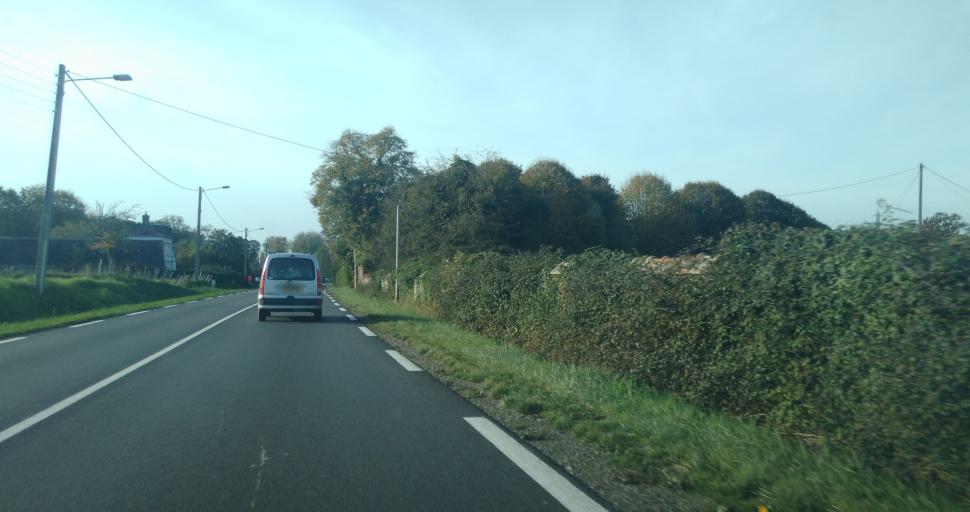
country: FR
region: Haute-Normandie
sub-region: Departement de l'Eure
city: Saint-Ouen-de-Thouberville
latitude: 49.3545
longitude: 0.9010
